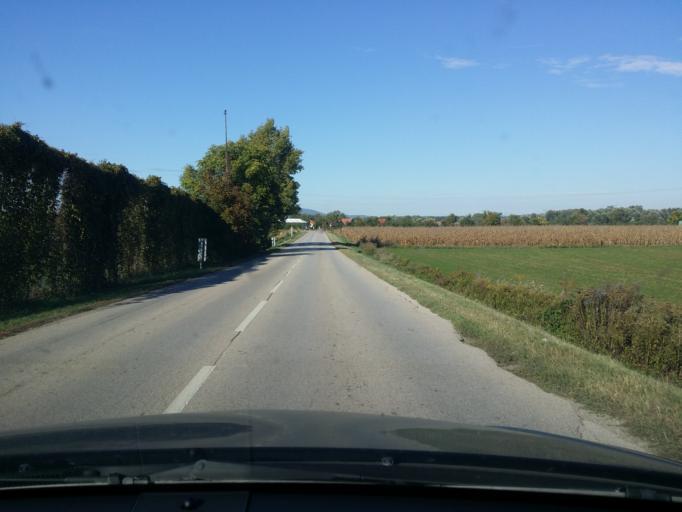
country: HU
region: Pest
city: God
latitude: 47.6948
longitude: 19.1568
